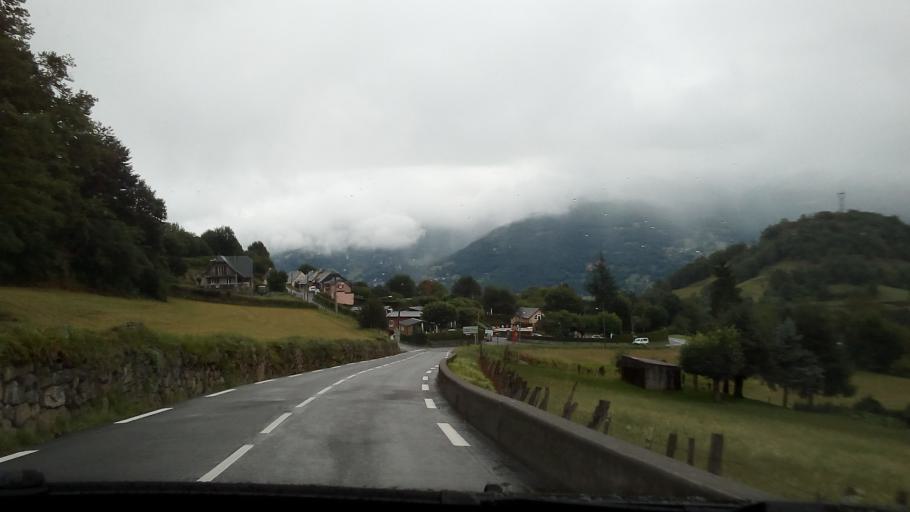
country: FR
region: Midi-Pyrenees
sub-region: Departement des Hautes-Pyrenees
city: Argeles-Gazost
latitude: 42.9947
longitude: -0.1230
